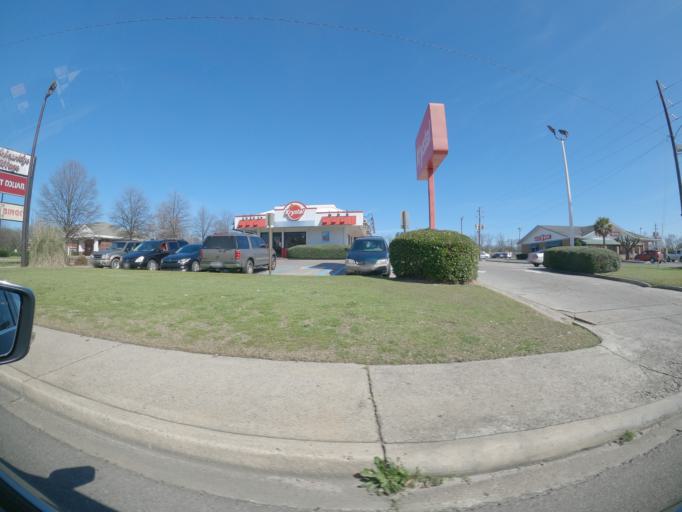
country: US
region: South Carolina
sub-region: Aiken County
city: North Augusta
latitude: 33.4908
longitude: -81.9527
